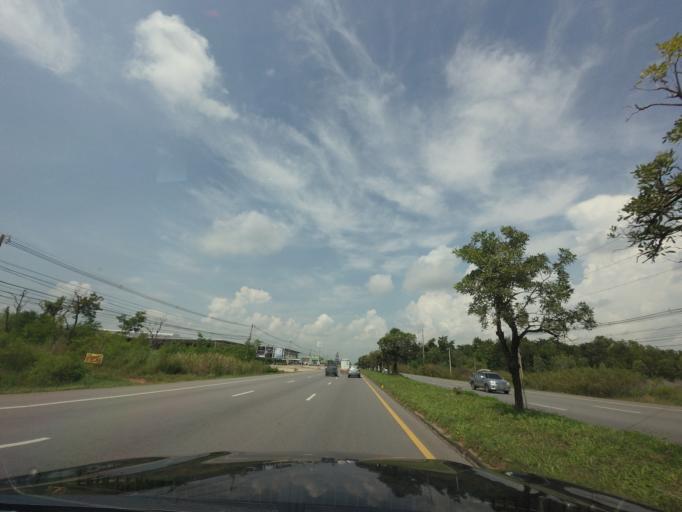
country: TH
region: Khon Kaen
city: Khon Kaen
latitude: 16.4507
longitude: 102.7435
